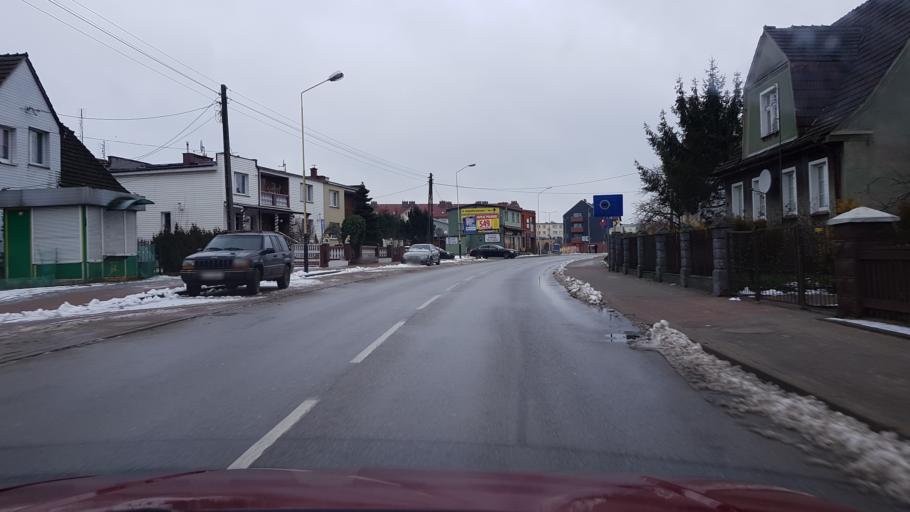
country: PL
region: West Pomeranian Voivodeship
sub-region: Powiat goleniowski
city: Nowogard
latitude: 53.6644
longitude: 15.1325
